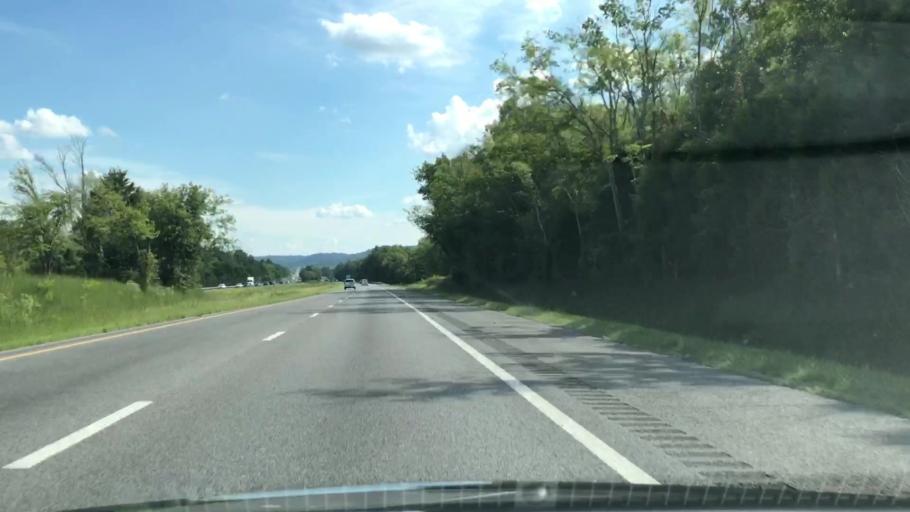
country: US
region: Tennessee
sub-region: Marshall County
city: Lewisburg
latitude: 35.4626
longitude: -86.8868
